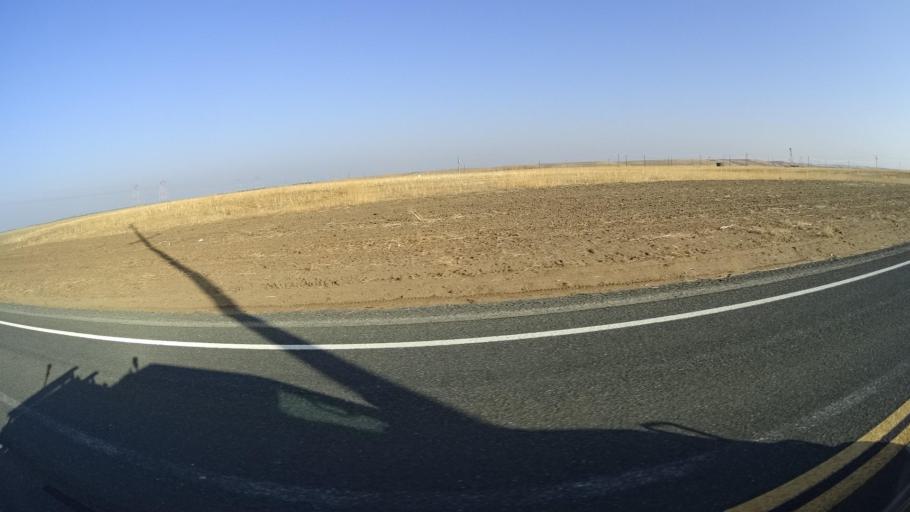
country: US
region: California
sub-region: Tulare County
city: Richgrove
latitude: 35.7620
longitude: -119.0621
